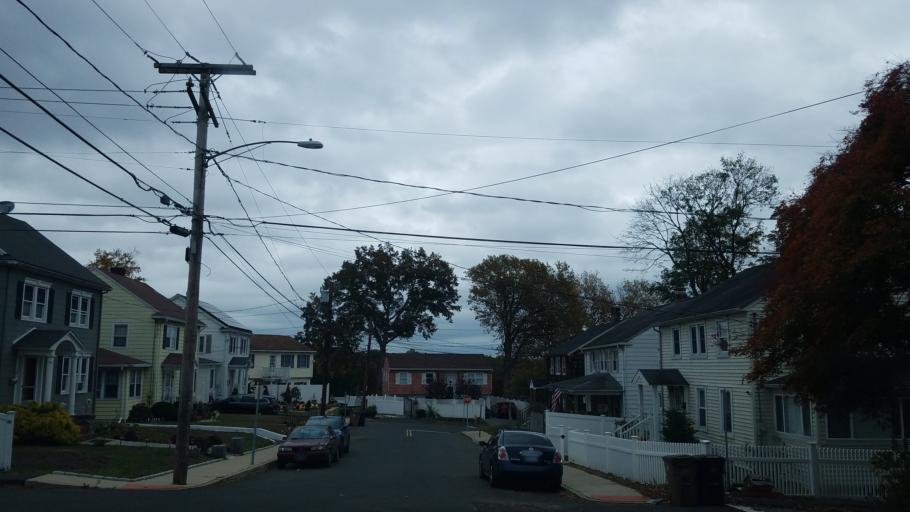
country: US
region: Connecticut
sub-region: Fairfield County
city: Stamford
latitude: 41.0575
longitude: -73.5101
